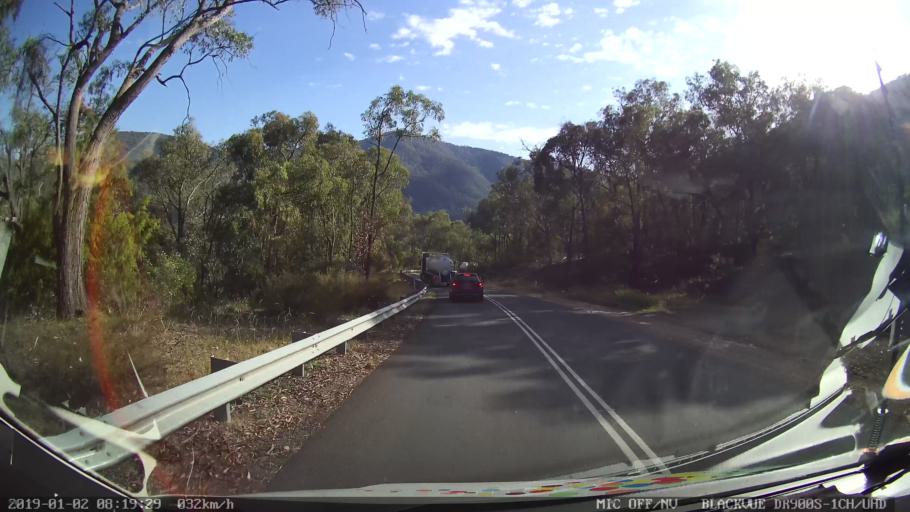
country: AU
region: New South Wales
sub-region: Tumut Shire
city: Tumut
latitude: -35.5749
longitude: 148.3217
